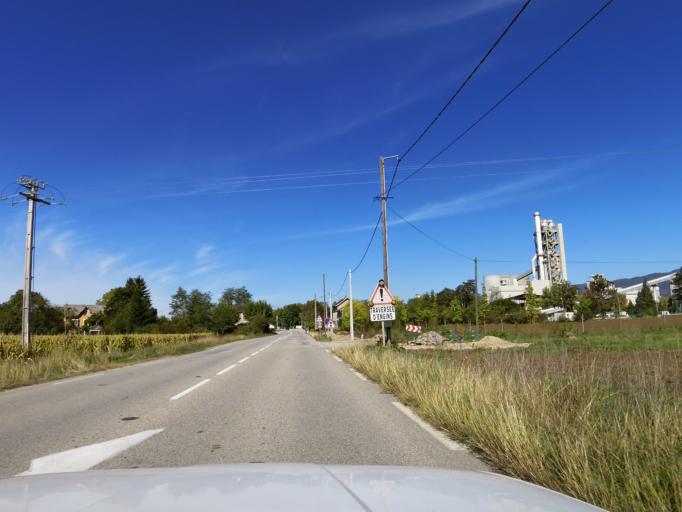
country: FR
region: Rhone-Alpes
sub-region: Departement de l'Isere
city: Bouvesse-Quirieu
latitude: 45.7993
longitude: 5.4216
